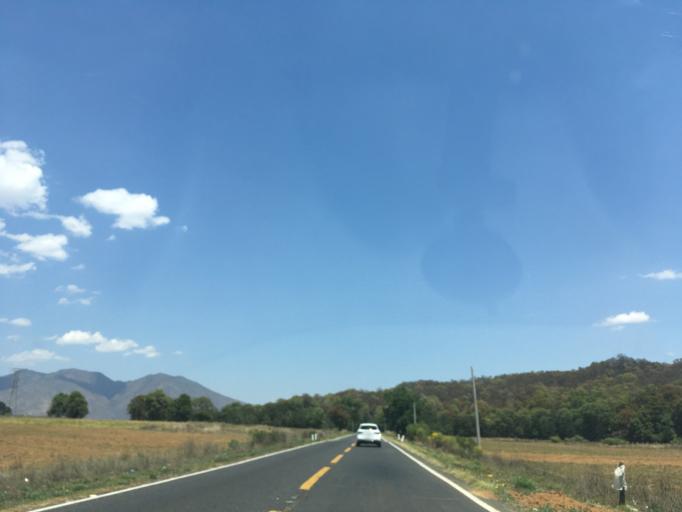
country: MX
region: Michoacan
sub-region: Chilchota
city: Tacuro (Santa Maria Tacuro)
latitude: 19.8191
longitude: -102.0277
